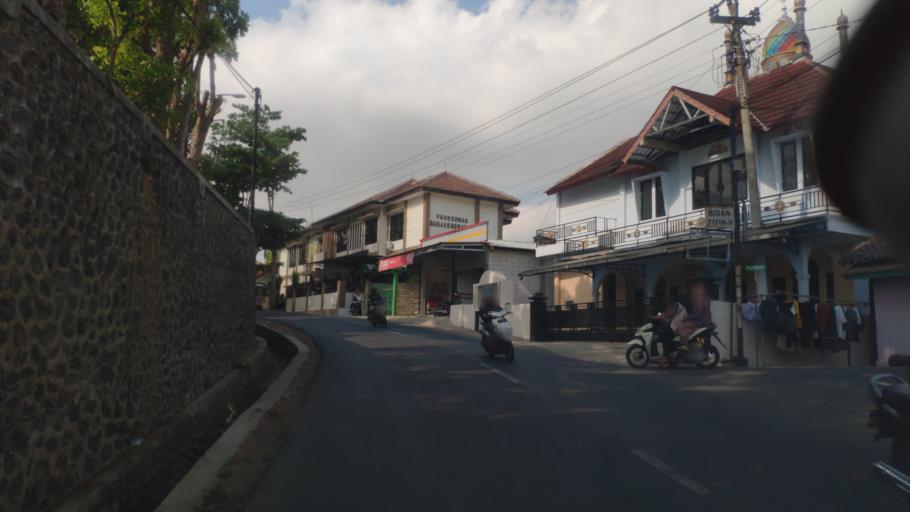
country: ID
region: Central Java
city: Wonosobo
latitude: -7.4069
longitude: 109.6828
